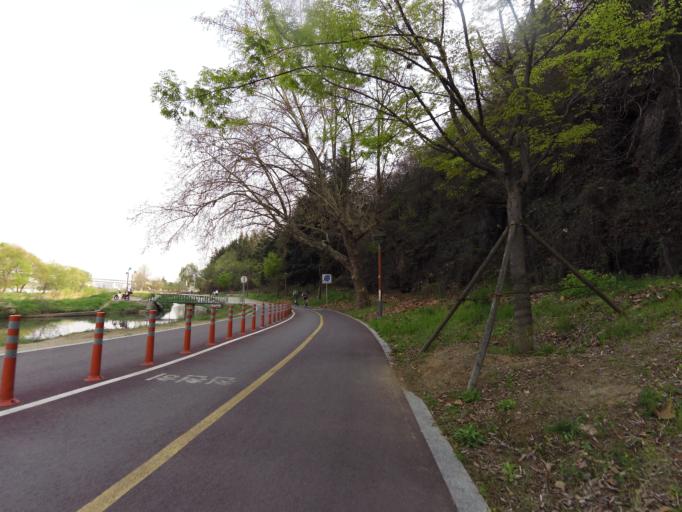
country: KR
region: Daegu
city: Daegu
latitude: 35.8862
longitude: 128.6449
